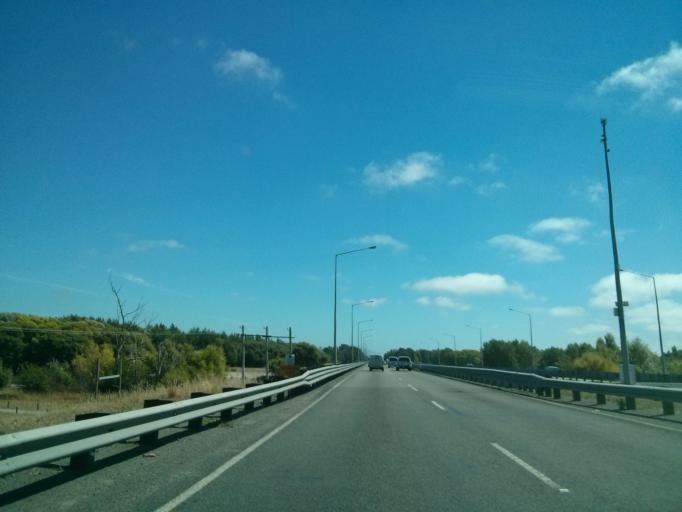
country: NZ
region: Canterbury
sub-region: Waimakariri District
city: Kaiapoi
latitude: -43.4169
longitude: 172.6471
